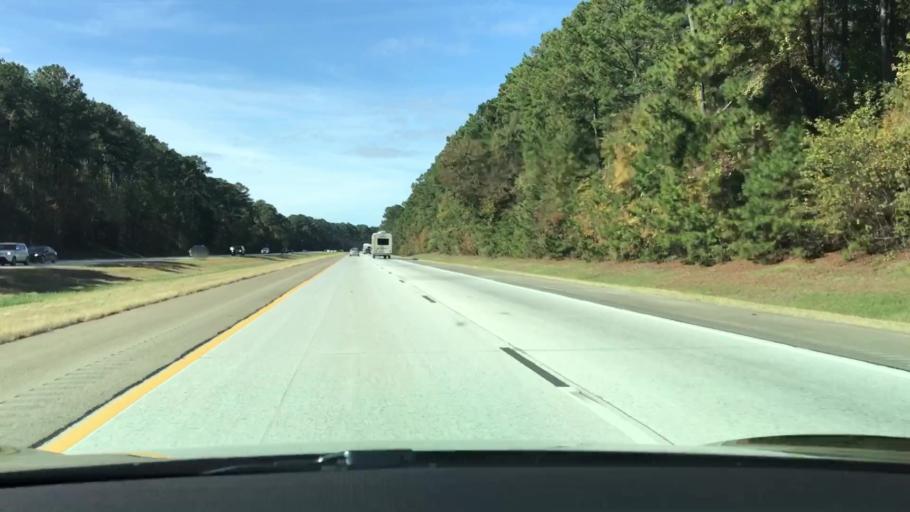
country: US
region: Georgia
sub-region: Putnam County
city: Jefferson
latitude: 33.5333
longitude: -83.2836
